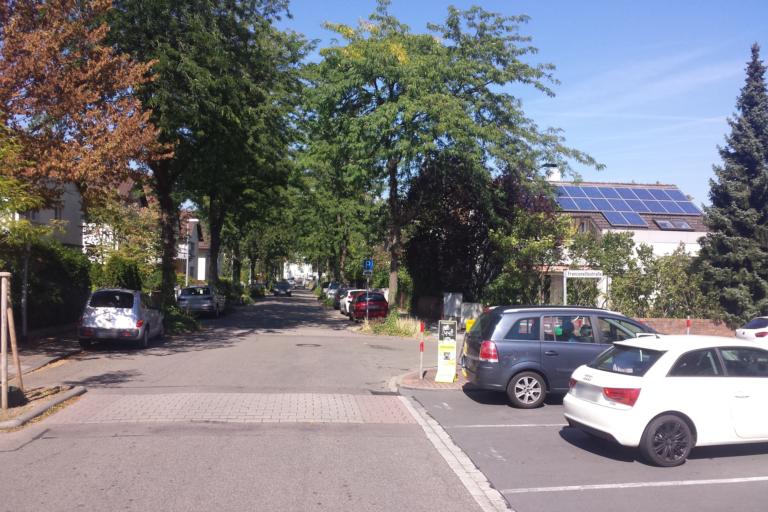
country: DE
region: Hesse
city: Viernheim
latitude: 49.5414
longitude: 8.5881
